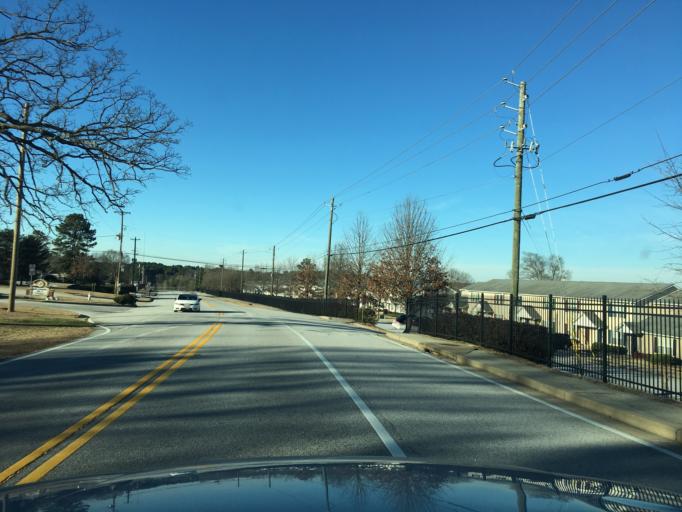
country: US
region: Georgia
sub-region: Rockdale County
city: Conyers
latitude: 33.6820
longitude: -84.0298
